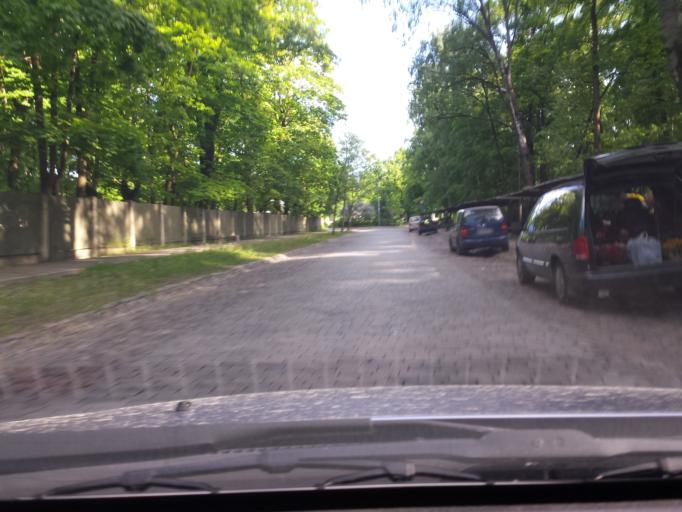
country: LV
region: Riga
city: Riga
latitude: 56.9831
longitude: 24.1486
